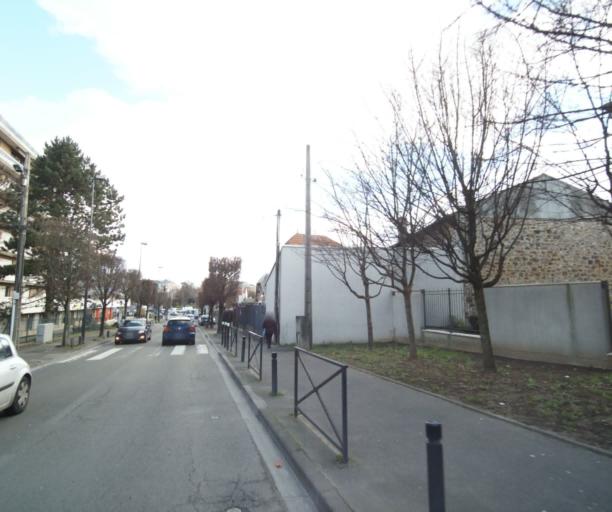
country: FR
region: Ile-de-France
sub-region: Departement de Seine-Saint-Denis
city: Pierrefitte-sur-Seine
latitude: 48.9633
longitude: 2.3572
